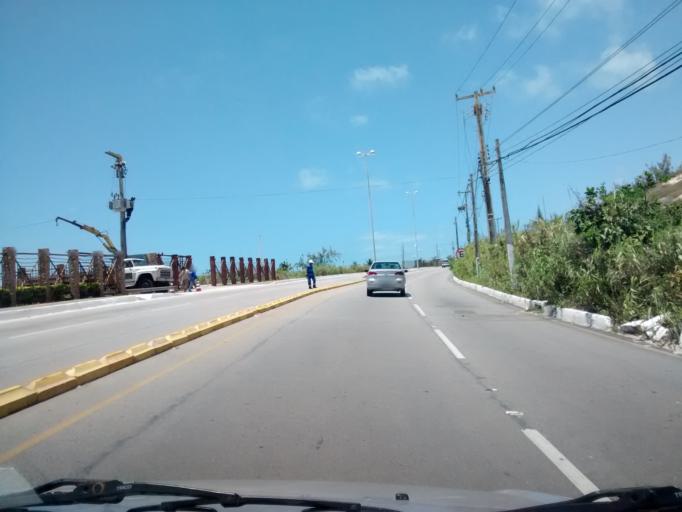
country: BR
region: Rio Grande do Norte
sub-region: Natal
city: Natal
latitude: -5.7941
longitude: -35.1845
